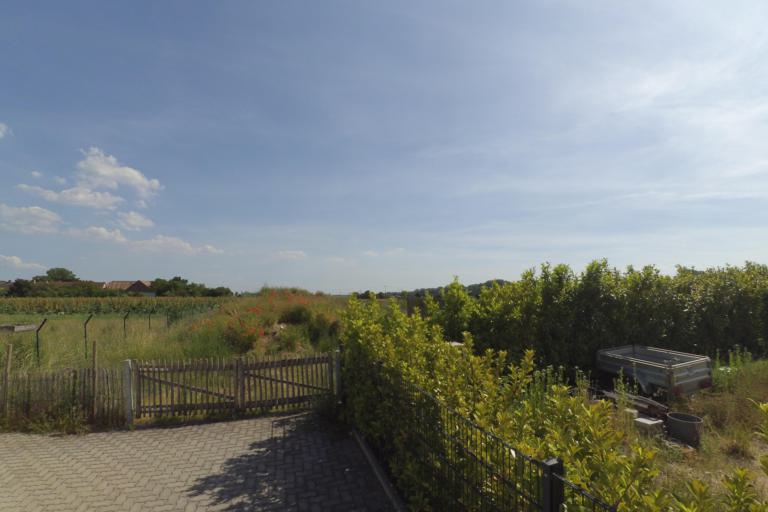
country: DE
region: Hesse
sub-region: Regierungsbezirk Darmstadt
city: Burstadt
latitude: 49.6301
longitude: 8.4778
